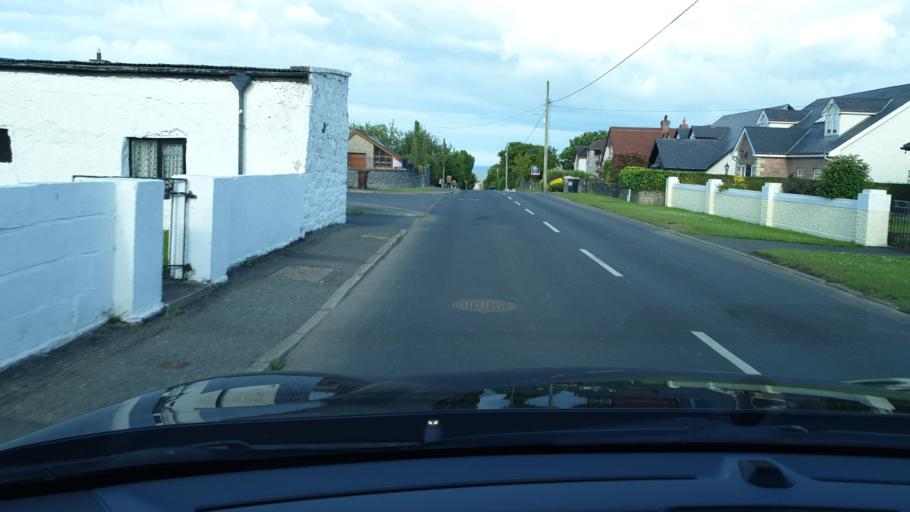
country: IE
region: Leinster
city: An Ros
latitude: 53.5470
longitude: -6.0963
